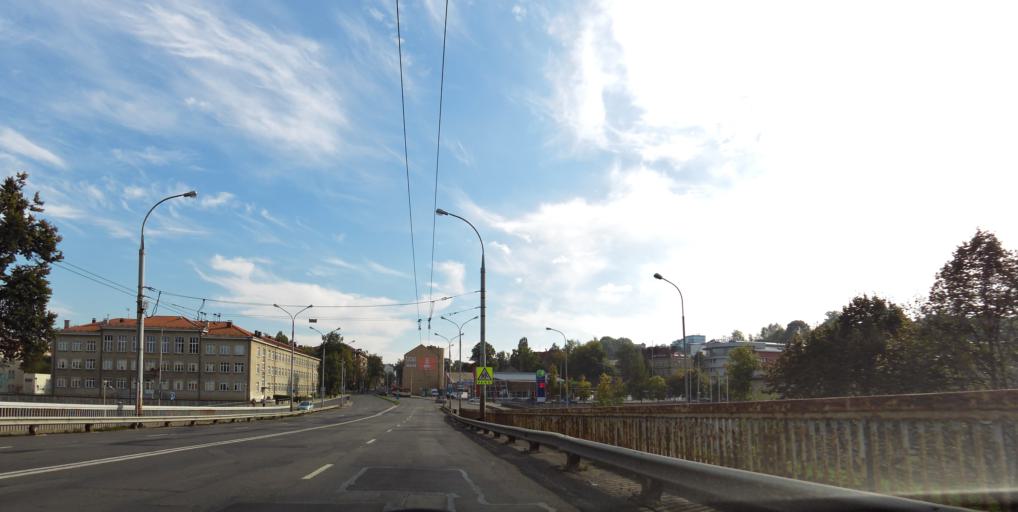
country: LT
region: Vilnius County
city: Naujamiestis
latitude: 54.6884
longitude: 25.2608
